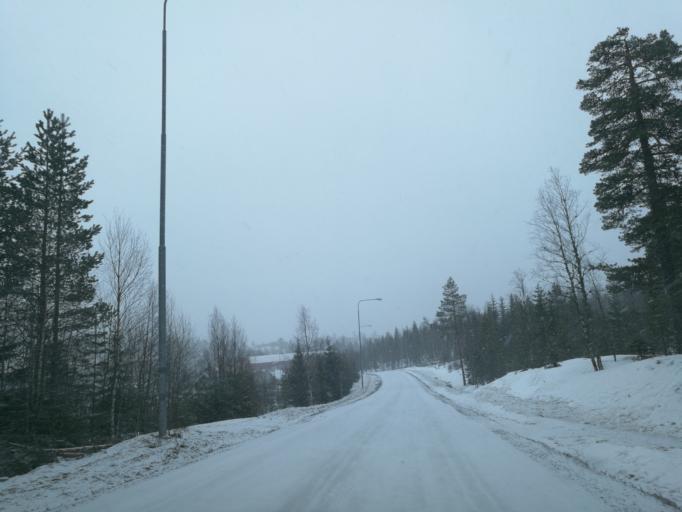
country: SE
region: Vaermland
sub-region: Torsby Kommun
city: Torsby
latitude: 60.6481
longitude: 12.9322
